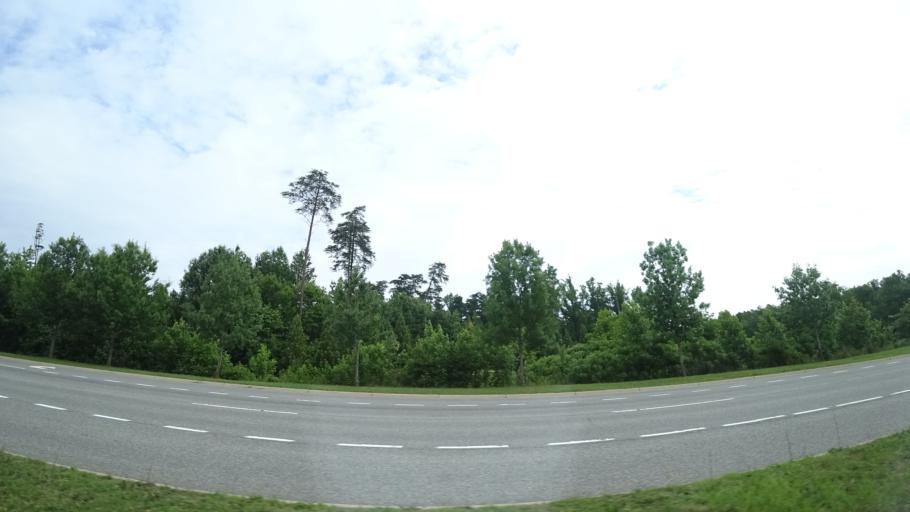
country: US
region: Virginia
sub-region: Spotsylvania County
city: Spotsylvania
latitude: 38.2061
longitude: -77.5969
